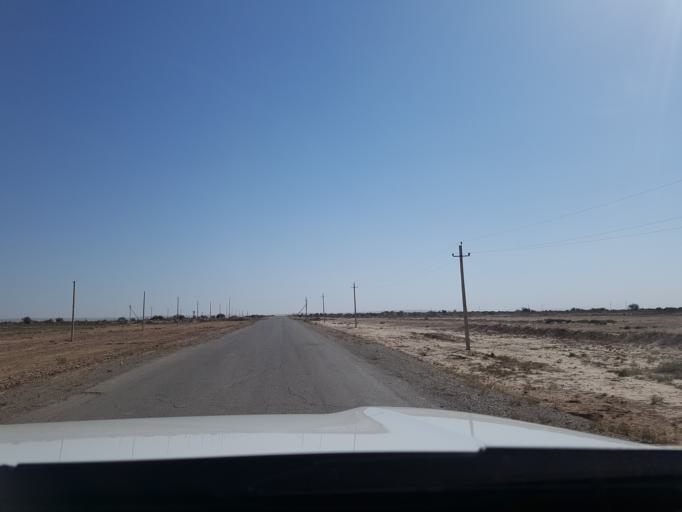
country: IR
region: Razavi Khorasan
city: Sarakhs
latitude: 36.5004
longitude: 61.2536
